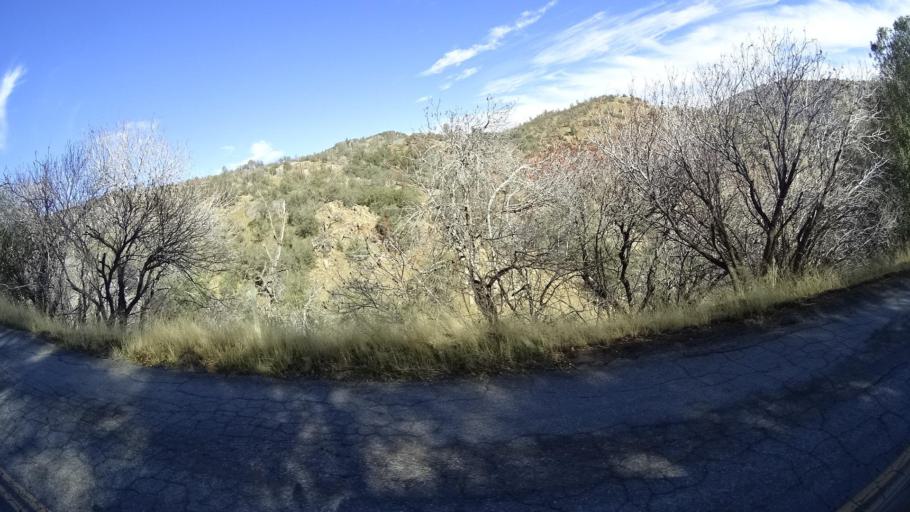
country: US
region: California
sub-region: Kern County
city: Alta Sierra
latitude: 35.6314
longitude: -118.7595
